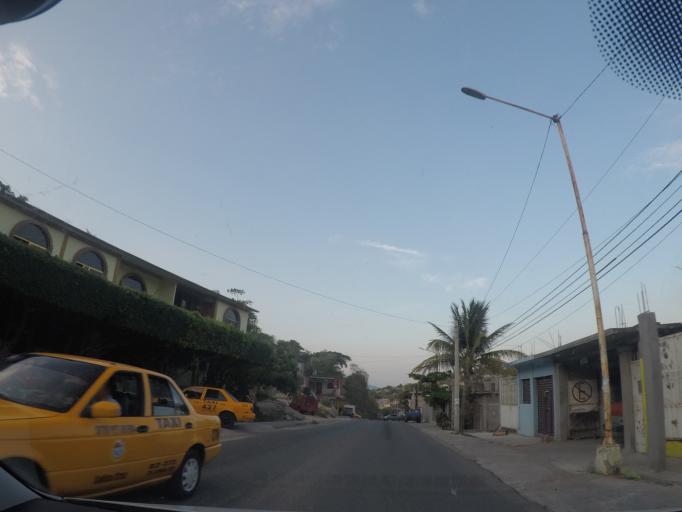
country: MX
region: Oaxaca
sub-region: Salina Cruz
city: Salina Cruz
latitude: 16.1935
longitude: -95.2063
